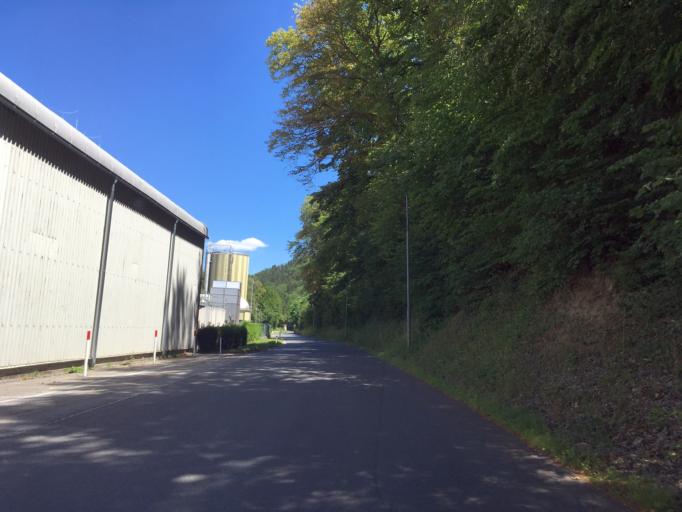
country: AT
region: Lower Austria
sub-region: Politischer Bezirk Neunkirchen
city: Pitten
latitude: 47.7070
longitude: 16.1775
